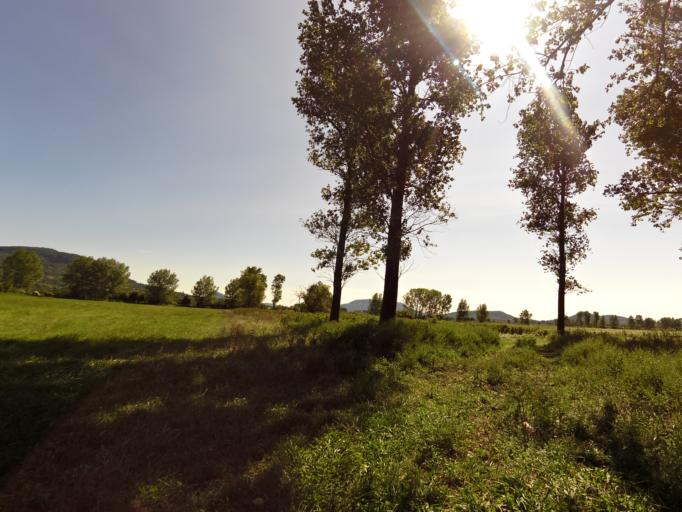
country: HU
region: Veszprem
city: Tapolca
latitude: 46.8324
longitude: 17.4129
